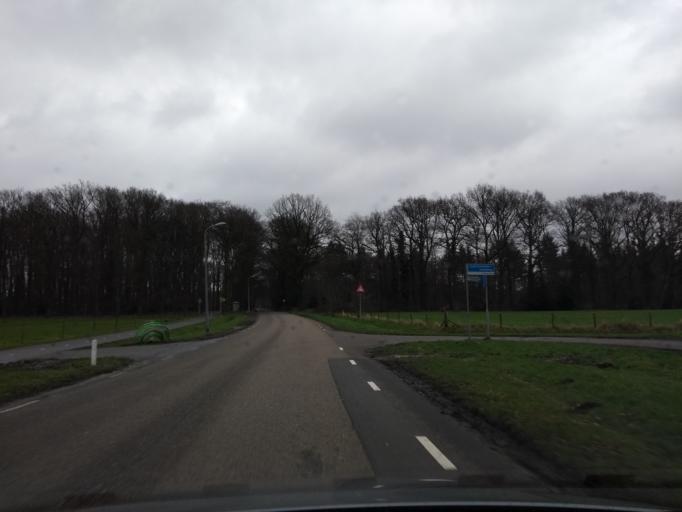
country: NL
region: Overijssel
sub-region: Gemeente Enschede
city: Enschede
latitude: 52.2038
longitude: 6.9251
